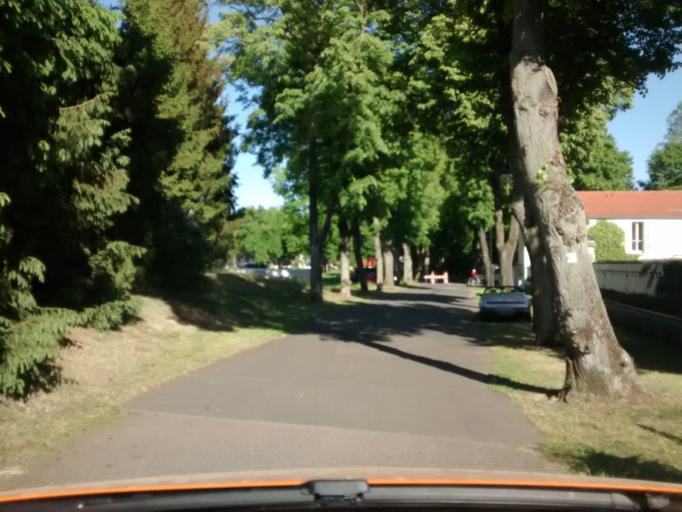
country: DE
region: Brandenburg
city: Bad Saarow
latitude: 52.2656
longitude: 14.0670
